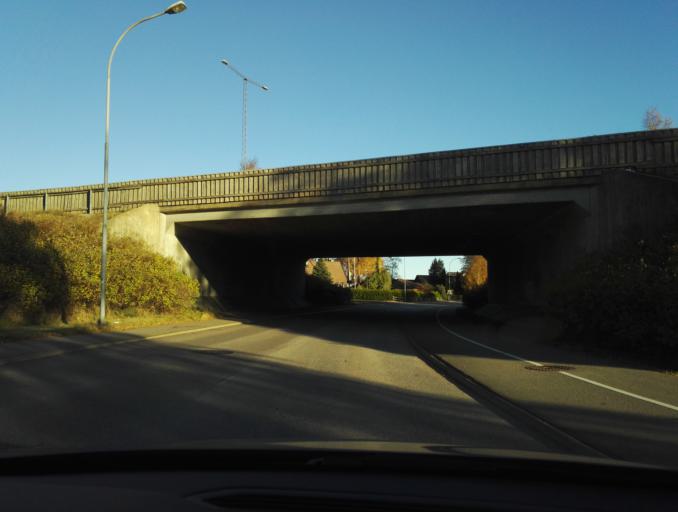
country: SE
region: Kronoberg
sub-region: Vaxjo Kommun
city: Vaexjoe
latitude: 56.8945
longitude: 14.7379
